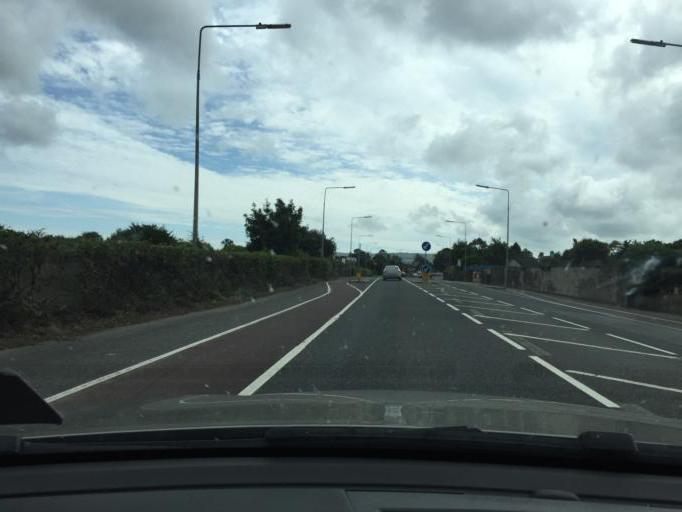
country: IE
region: Munster
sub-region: Waterford
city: Dungarvan
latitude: 52.1008
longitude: -7.6065
